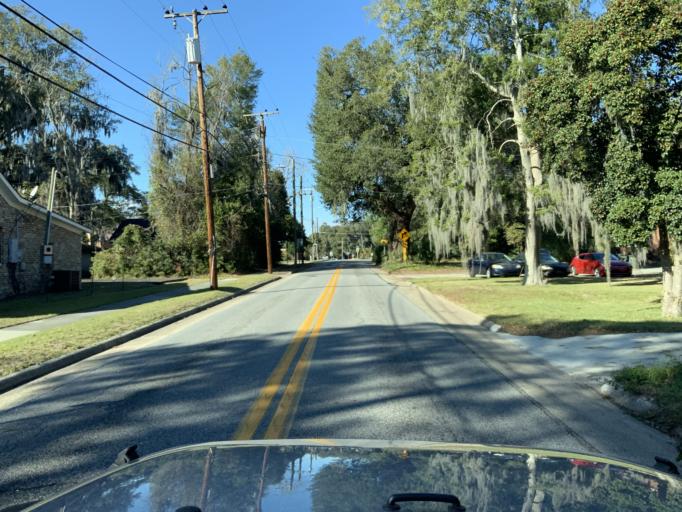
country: US
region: Georgia
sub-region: Chatham County
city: Thunderbolt
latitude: 32.0588
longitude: -81.0694
